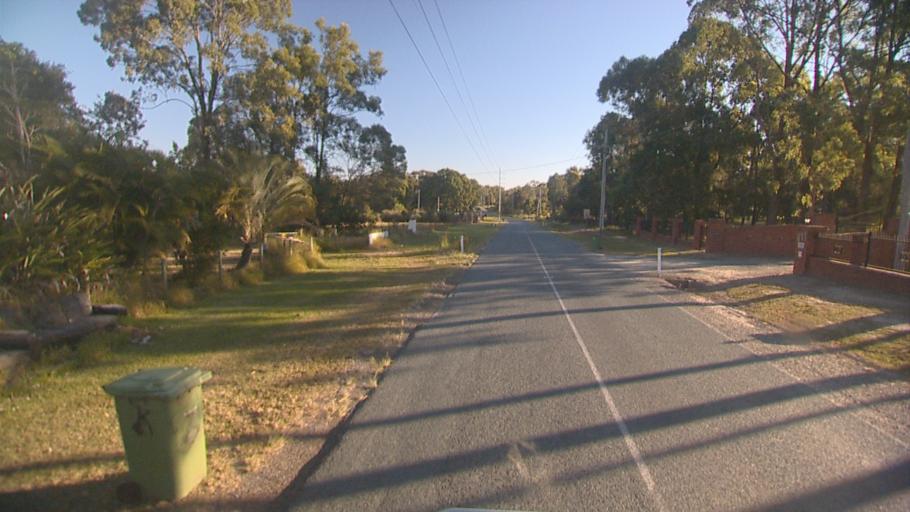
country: AU
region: Queensland
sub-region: Logan
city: Logan Reserve
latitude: -27.7267
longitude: 153.0994
